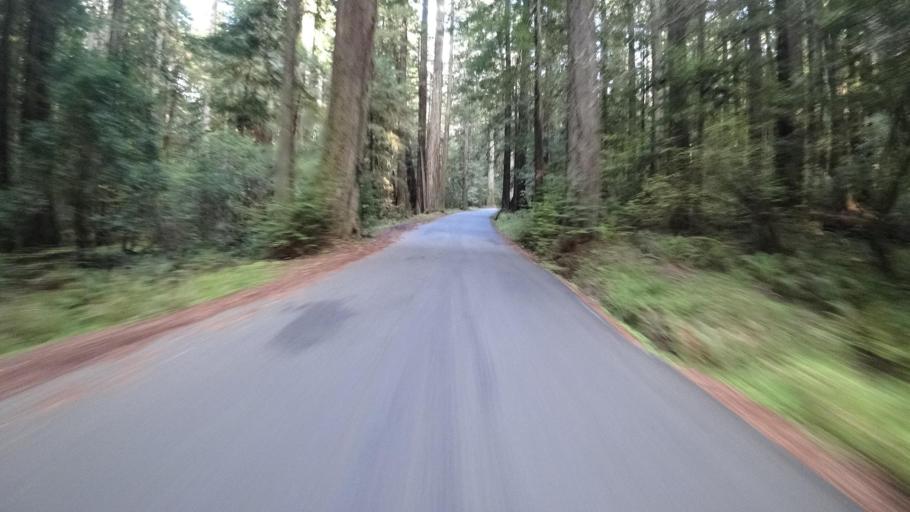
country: US
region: California
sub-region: Humboldt County
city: Rio Dell
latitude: 40.3484
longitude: -123.9576
